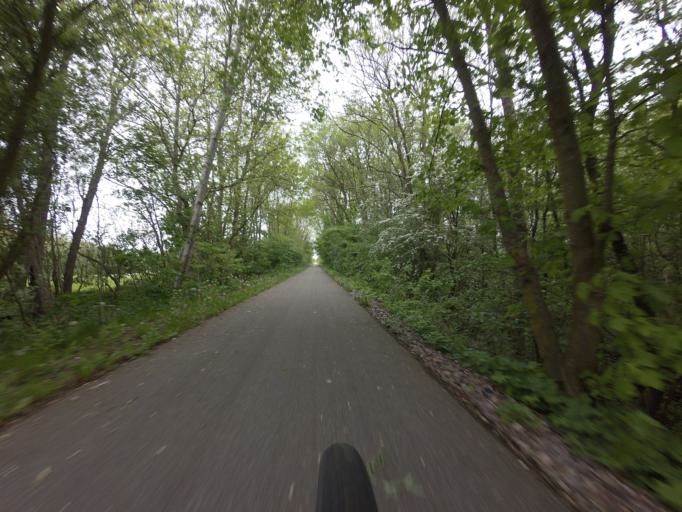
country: DK
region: Zealand
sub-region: Slagelse Kommune
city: Slagelse
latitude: 55.3170
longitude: 11.4083
